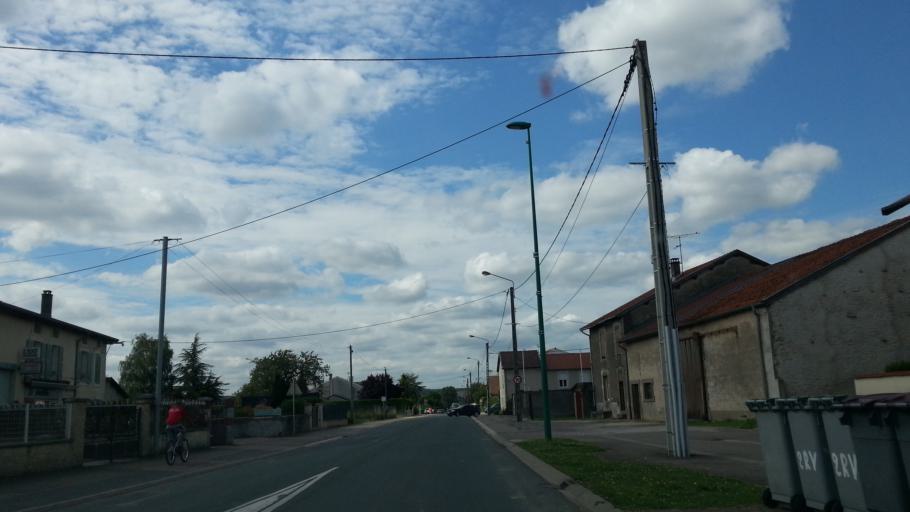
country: FR
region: Lorraine
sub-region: Departement de la Meuse
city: Thierville-sur-Meuse
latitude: 49.1702
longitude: 5.3518
